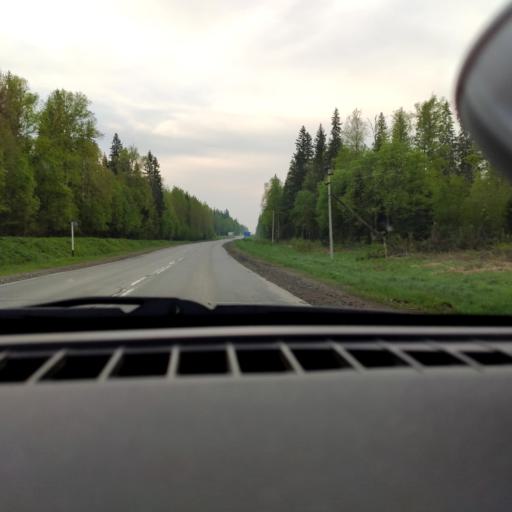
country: RU
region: Perm
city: Perm
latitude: 58.2012
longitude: 56.2048
